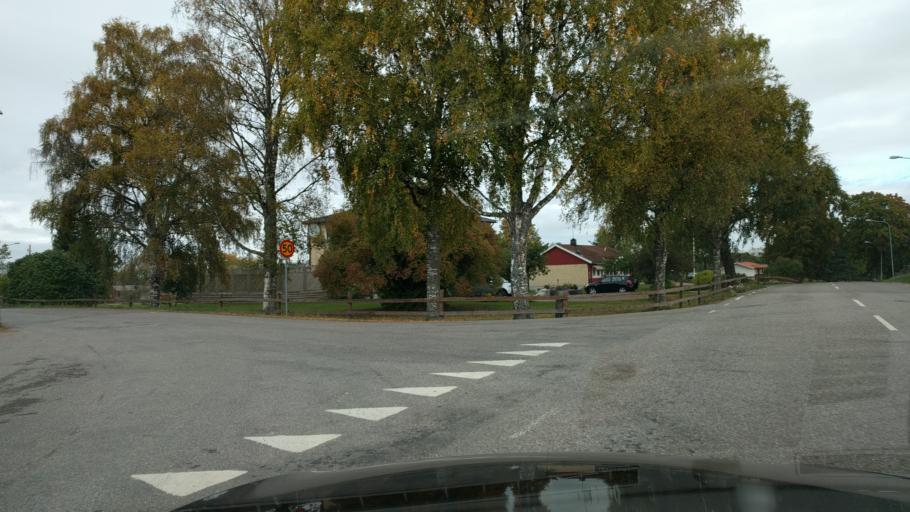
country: SE
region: Uppsala
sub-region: Osthammars Kommun
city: Bjorklinge
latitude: 60.1443
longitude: 17.5760
